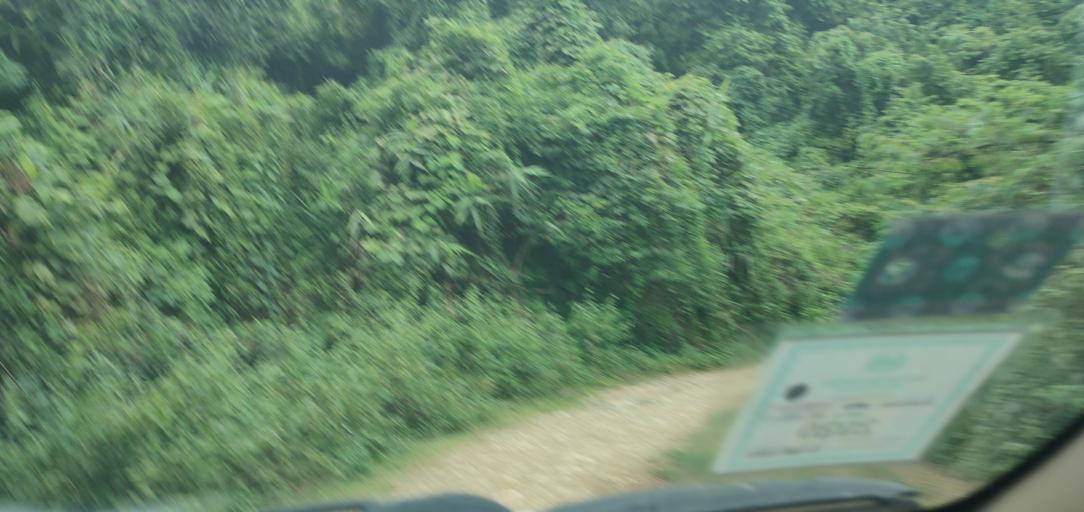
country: LA
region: Phongsali
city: Phongsali
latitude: 21.4416
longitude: 102.3223
